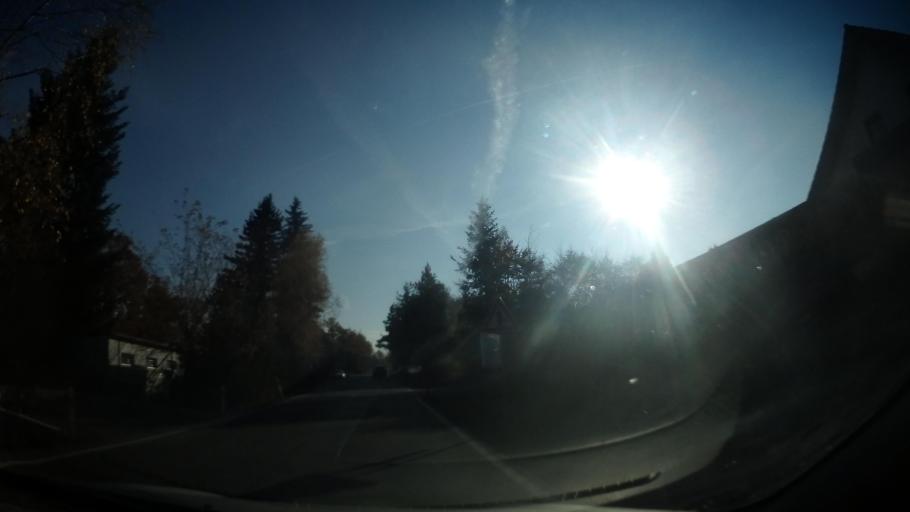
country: CZ
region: Central Bohemia
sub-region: Okres Praha-Vychod
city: Mnichovice
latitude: 49.9145
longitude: 14.7238
